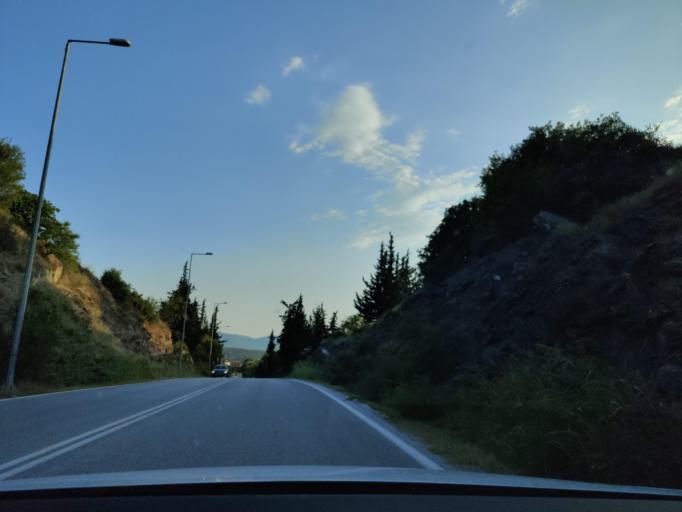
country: GR
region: East Macedonia and Thrace
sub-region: Nomos Kavalas
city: Zygos
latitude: 40.9929
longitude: 24.3790
